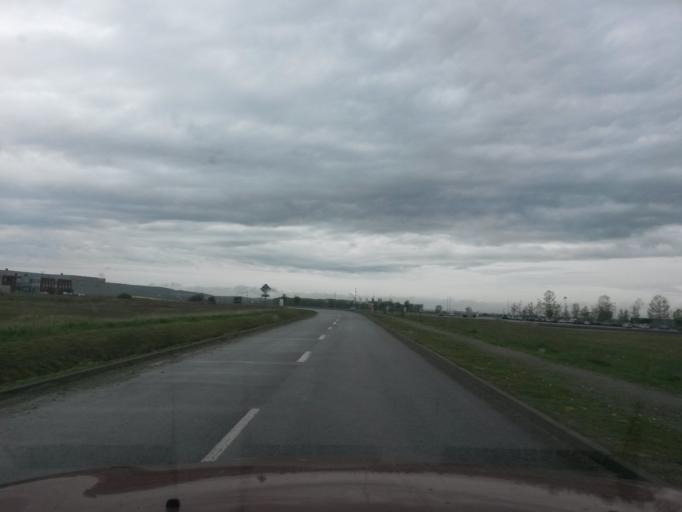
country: HU
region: Borsod-Abauj-Zemplen
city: Gonc
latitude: 48.5486
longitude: 21.2298
